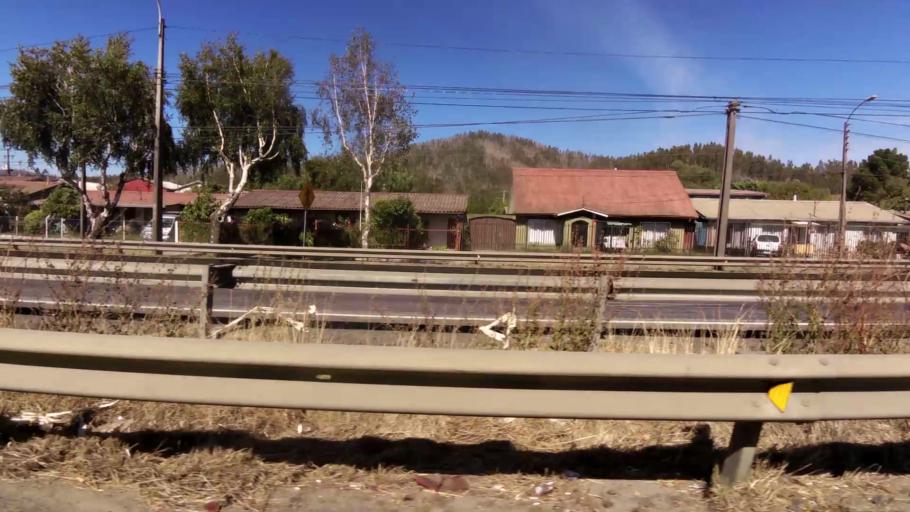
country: CL
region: Biobio
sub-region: Provincia de Concepcion
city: Concepcion
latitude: -36.7925
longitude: -73.0254
